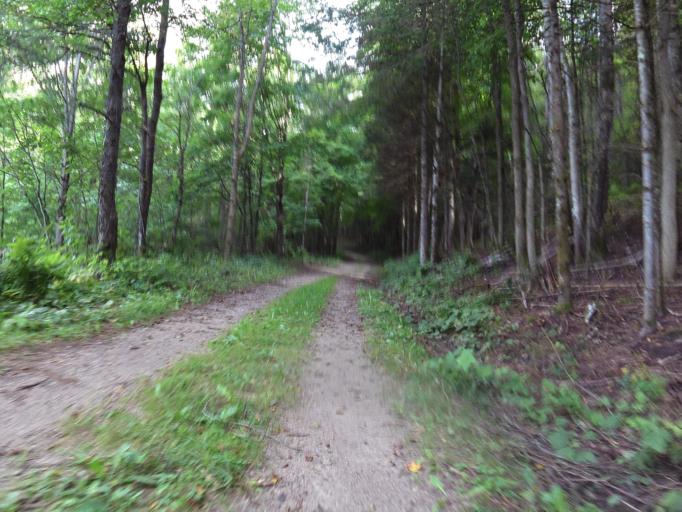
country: CA
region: Quebec
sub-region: Outaouais
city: Wakefield
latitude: 45.6364
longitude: -75.9897
